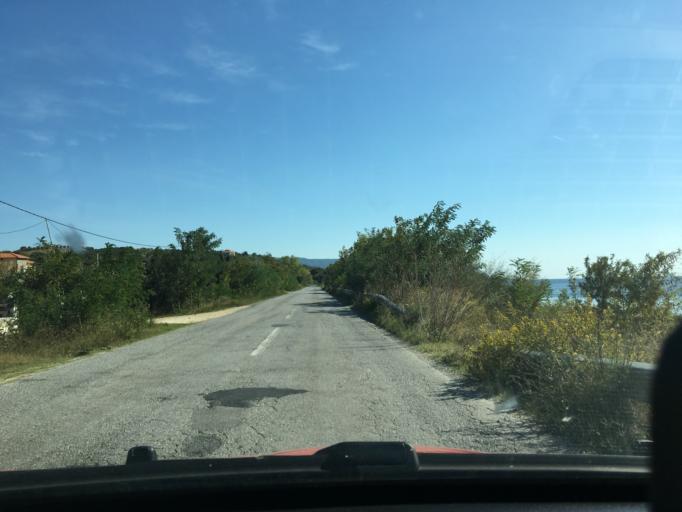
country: GR
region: Central Macedonia
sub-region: Nomos Chalkidikis
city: Nea Roda
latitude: 40.3632
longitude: 23.9253
